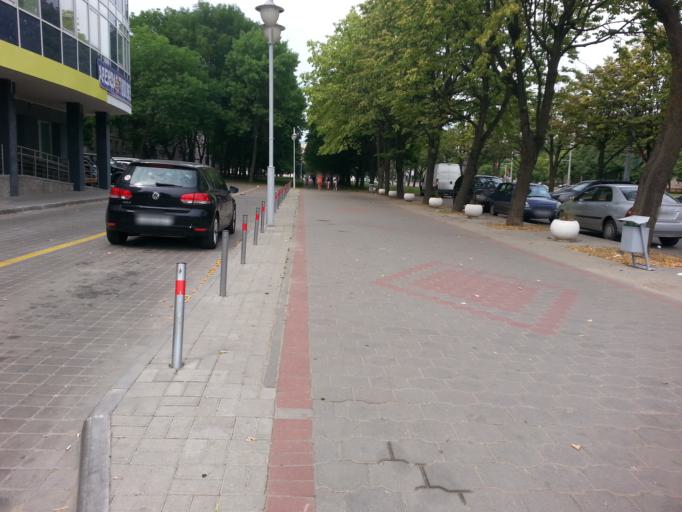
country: BY
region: Minsk
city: Novoye Medvezhino
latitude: 53.9108
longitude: 27.4948
